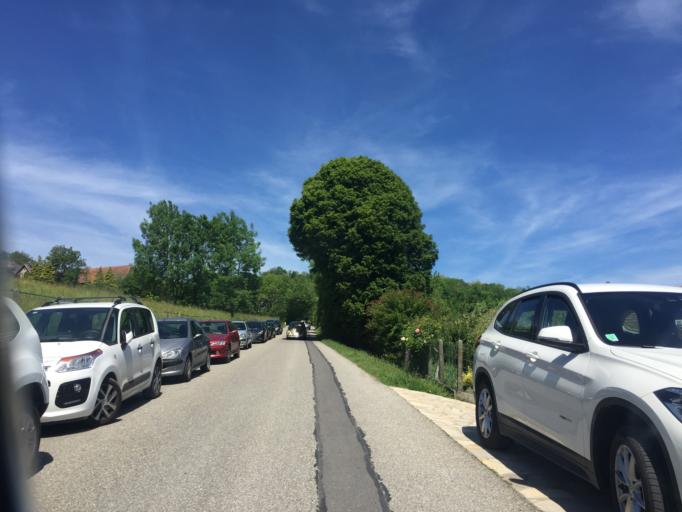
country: FR
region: Rhone-Alpes
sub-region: Departement de la Haute-Savoie
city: Sillingy
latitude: 45.9285
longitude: 5.9977
